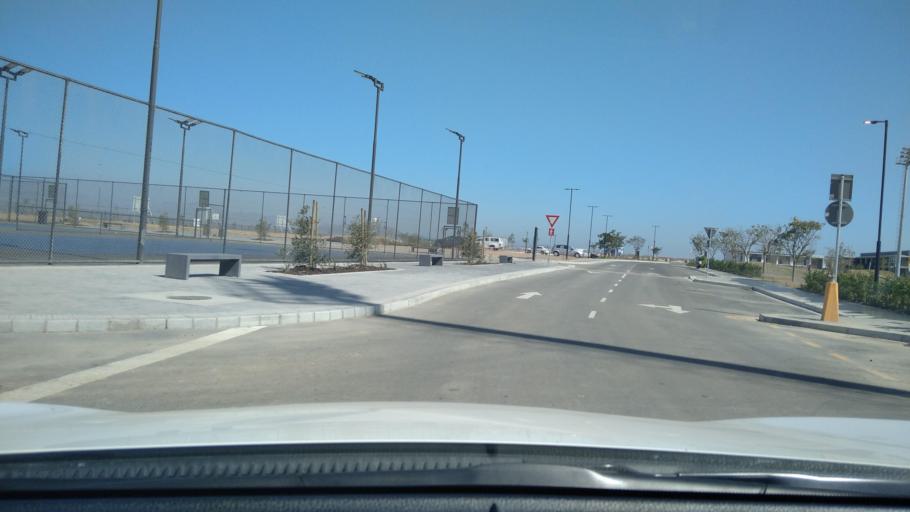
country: ZA
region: Western Cape
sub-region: City of Cape Town
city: Kraaifontein
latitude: -33.8045
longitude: 18.6919
